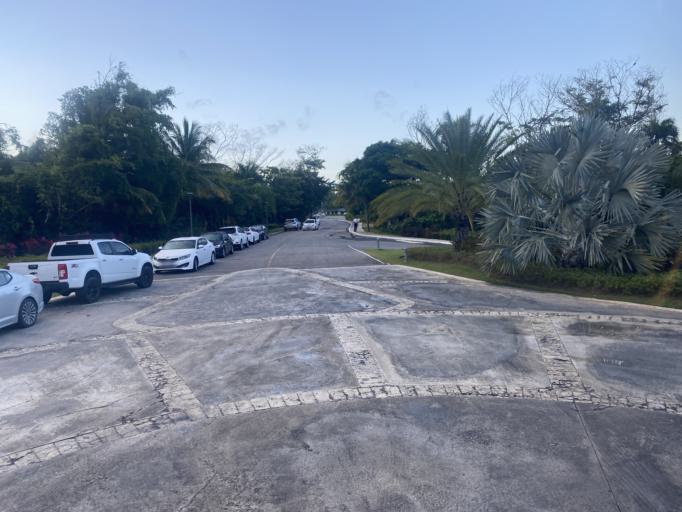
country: DO
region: San Juan
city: Punta Cana
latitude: 18.7316
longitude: -68.4690
